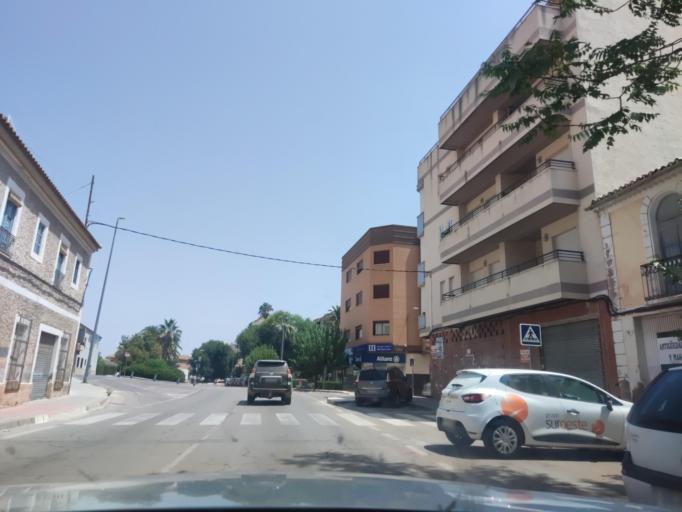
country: ES
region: Castille-La Mancha
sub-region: Provincia de Albacete
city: Hellin
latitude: 38.5102
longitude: -1.6944
